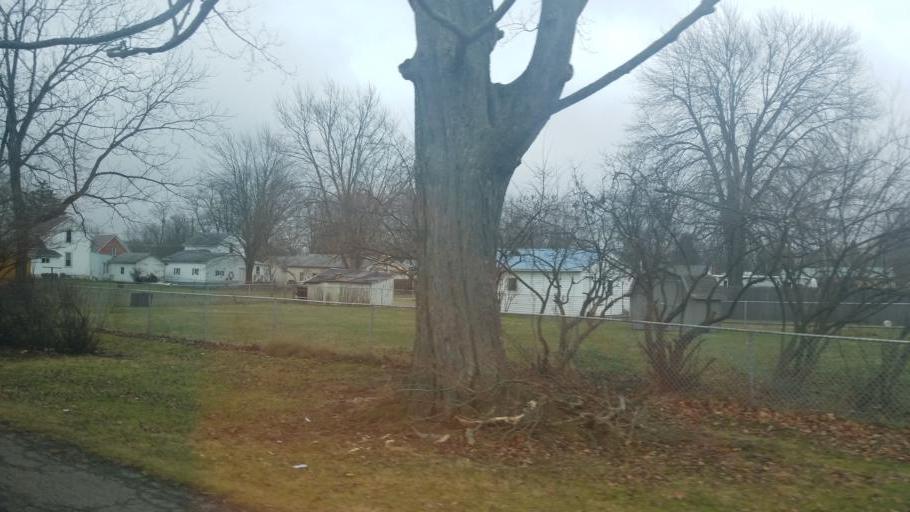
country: US
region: Ohio
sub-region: Crawford County
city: Galion
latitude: 40.7323
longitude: -82.7725
